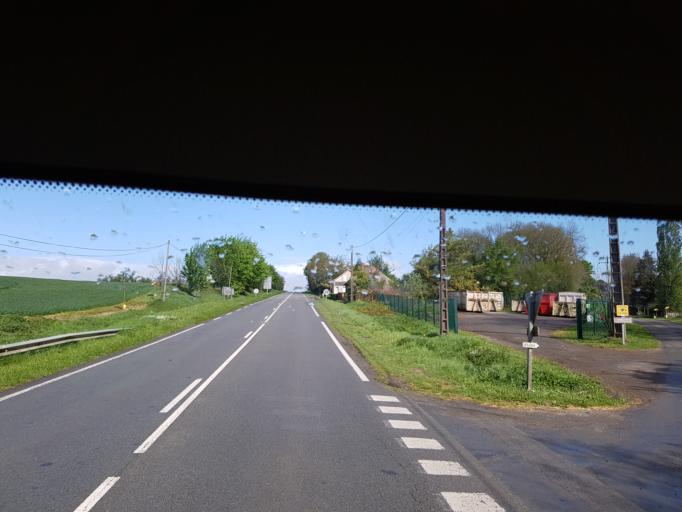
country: FR
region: Picardie
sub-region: Departement de l'Aisne
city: Beaurevoir
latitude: 49.9535
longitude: 3.2350
